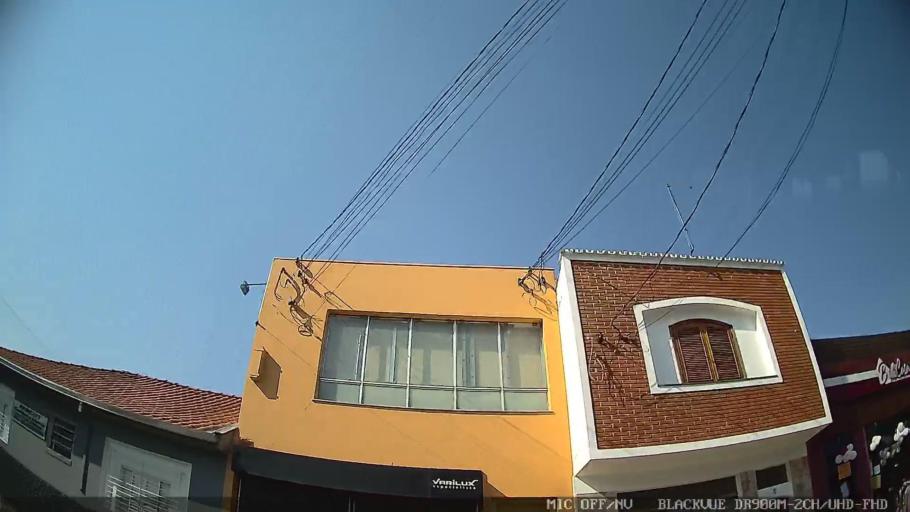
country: BR
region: Sao Paulo
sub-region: Itatiba
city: Itatiba
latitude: -23.0039
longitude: -46.8443
